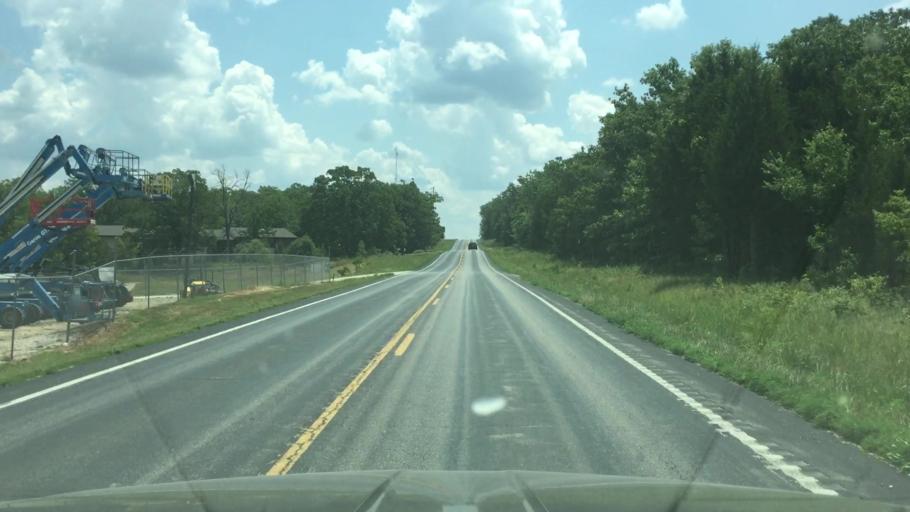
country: US
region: Missouri
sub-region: Camden County
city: Osage Beach
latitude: 38.1388
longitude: -92.5796
